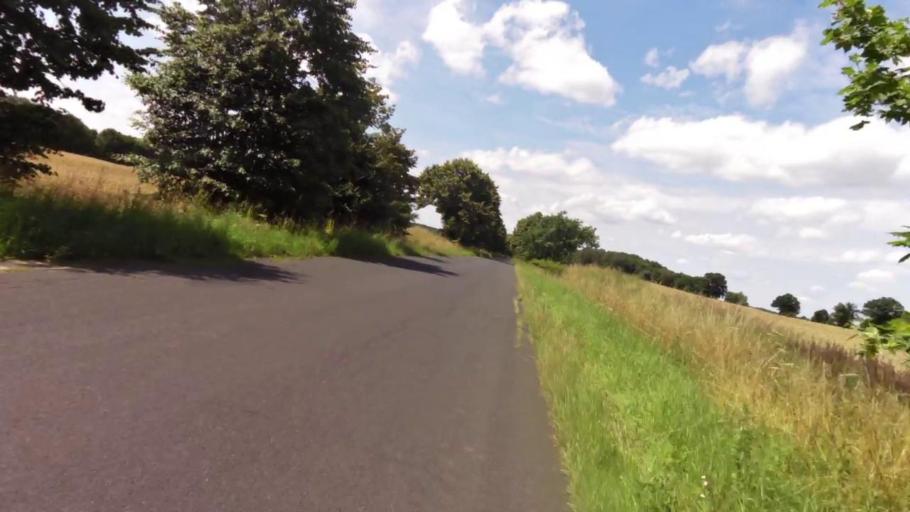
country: PL
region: West Pomeranian Voivodeship
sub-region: Powiat stargardzki
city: Dobrzany
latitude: 53.4289
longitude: 15.4375
